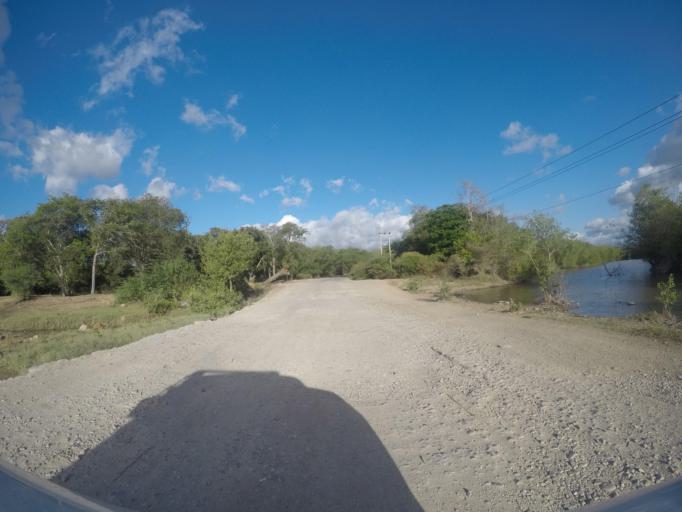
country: TL
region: Lautem
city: Lospalos
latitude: -8.3718
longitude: 126.8842
